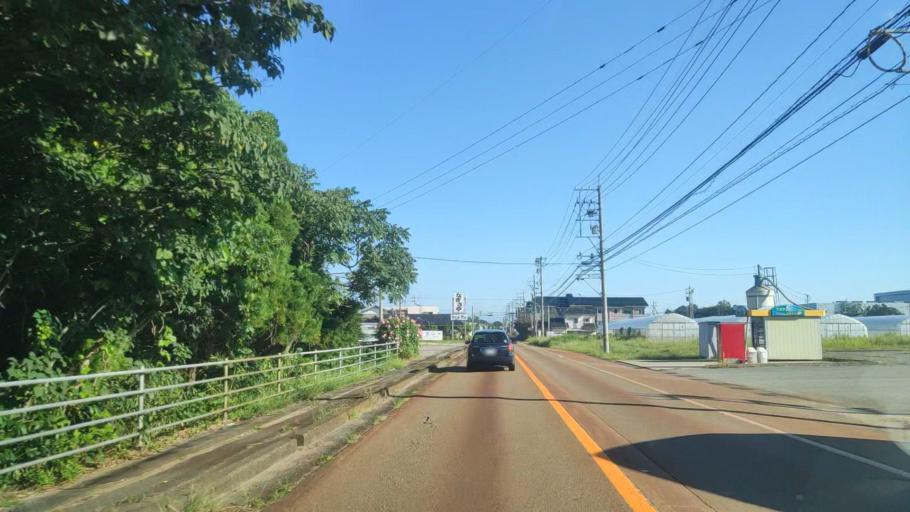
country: JP
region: Ishikawa
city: Hakui
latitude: 36.8507
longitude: 136.7692
